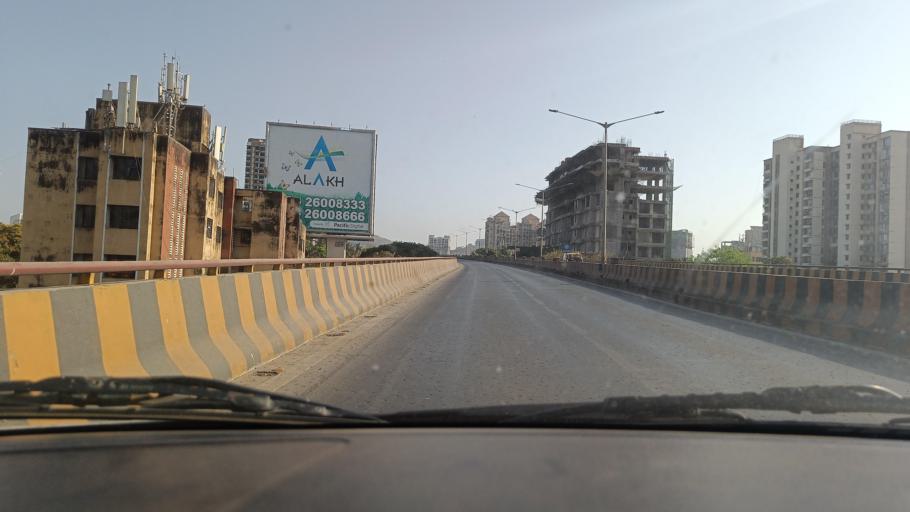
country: IN
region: Maharashtra
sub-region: Mumbai Suburban
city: Mumbai
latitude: 19.0546
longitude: 72.9110
